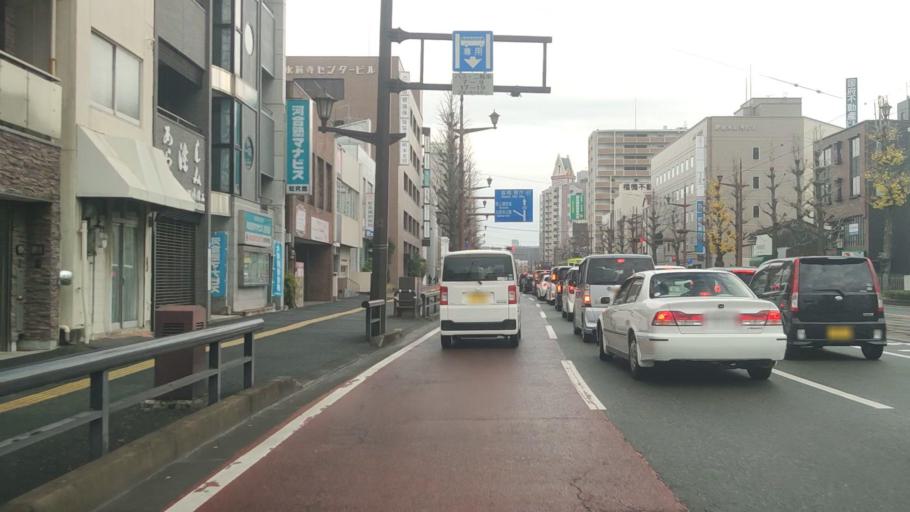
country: JP
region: Kumamoto
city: Kumamoto
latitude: 32.7928
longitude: 130.7283
